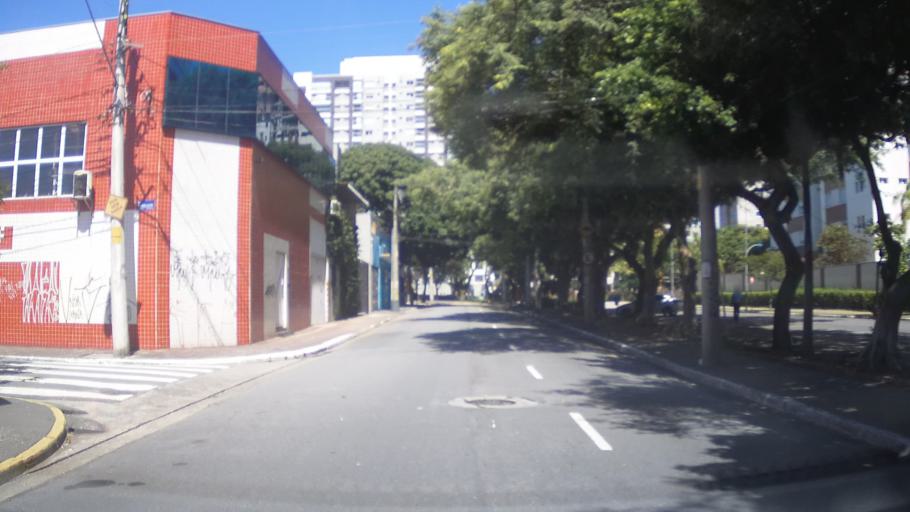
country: BR
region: Sao Paulo
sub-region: Sao Caetano Do Sul
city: Sao Caetano do Sul
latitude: -23.6247
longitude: -46.5772
